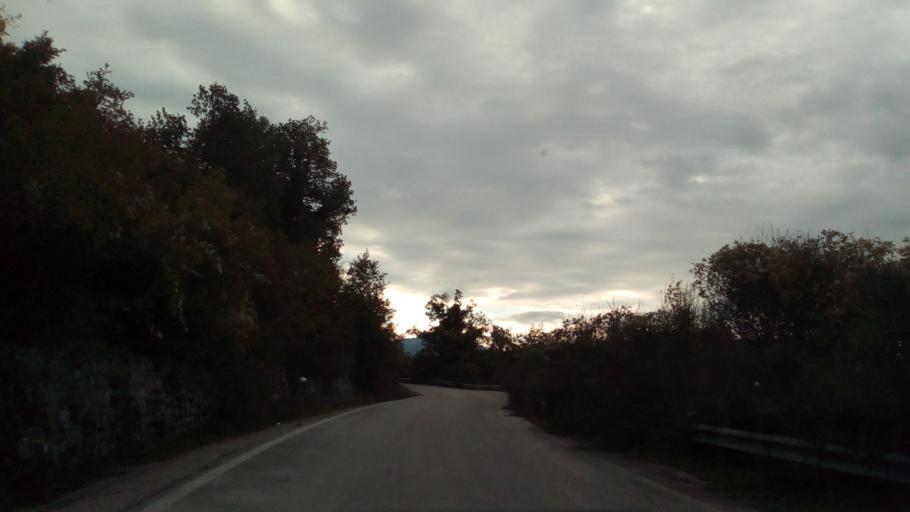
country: GR
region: West Greece
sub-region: Nomos Aitolias kai Akarnanias
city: Thermo
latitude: 38.6058
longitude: 21.7958
